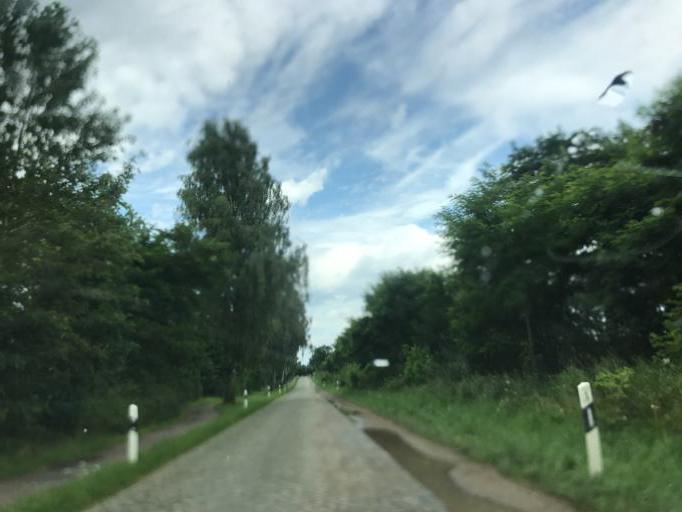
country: DE
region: Mecklenburg-Vorpommern
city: Mollenhagen
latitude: 53.4159
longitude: 12.9195
